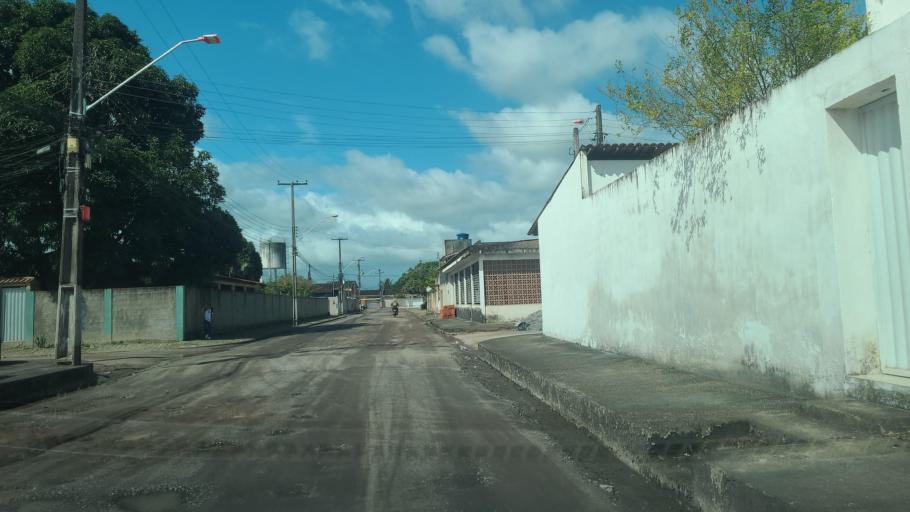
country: BR
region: Alagoas
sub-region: Satuba
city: Satuba
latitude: -9.5179
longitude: -35.8066
